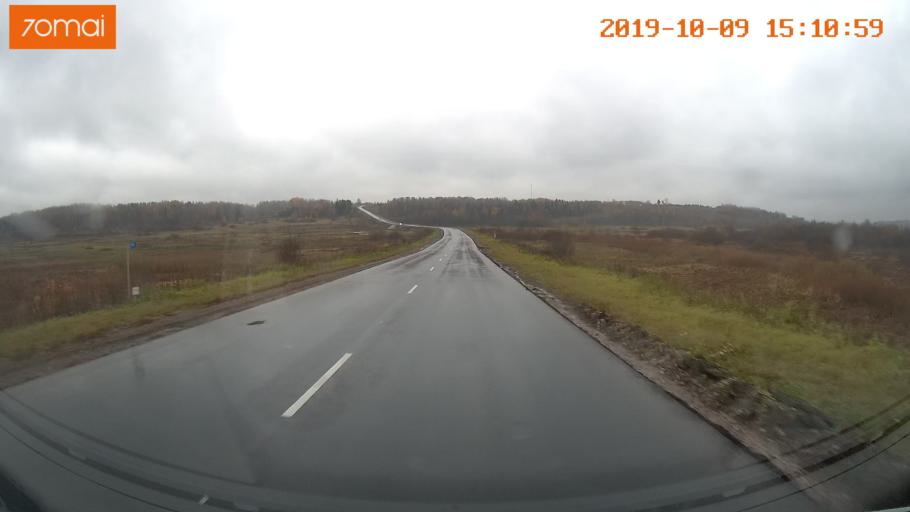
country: RU
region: Kostroma
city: Susanino
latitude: 58.1711
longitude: 41.6336
